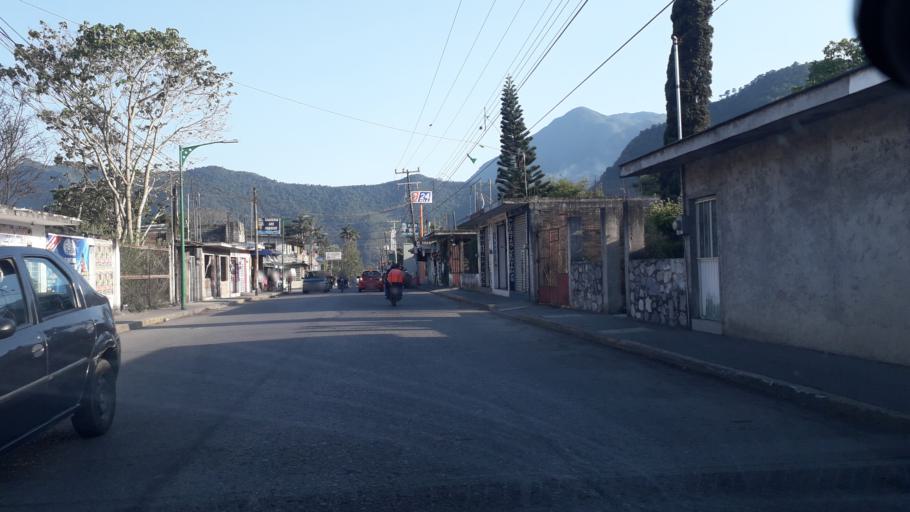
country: MX
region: Veracruz
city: Jalapilla
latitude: 18.8260
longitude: -97.0900
